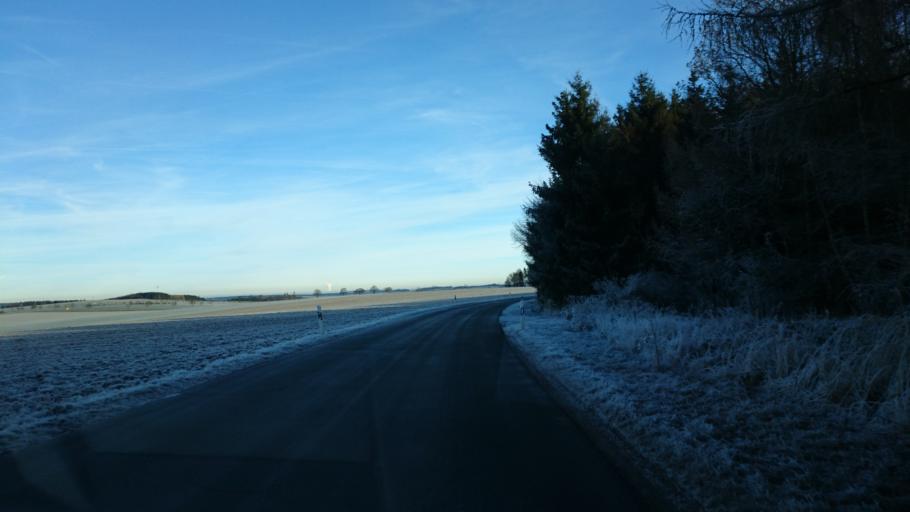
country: DE
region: Thuringia
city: Tanna
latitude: 50.5189
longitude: 11.8738
